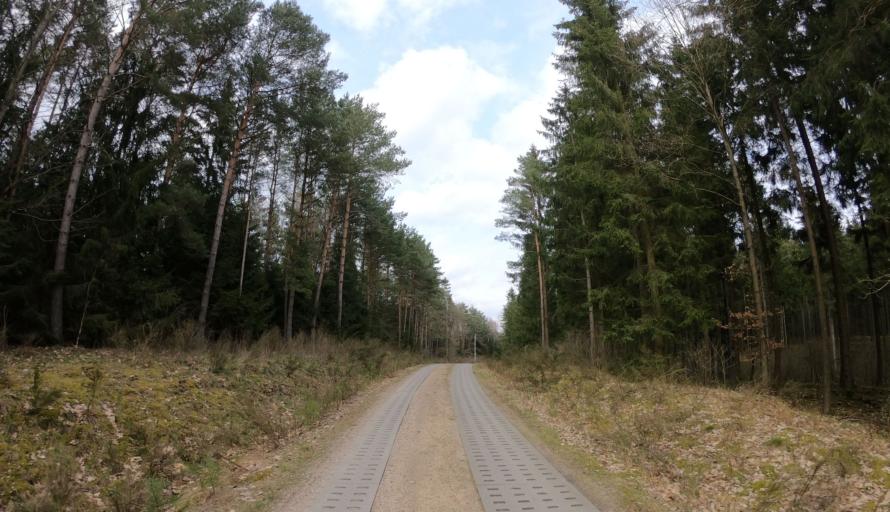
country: PL
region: West Pomeranian Voivodeship
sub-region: Powiat swidwinski
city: Rabino
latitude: 53.8679
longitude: 15.8725
